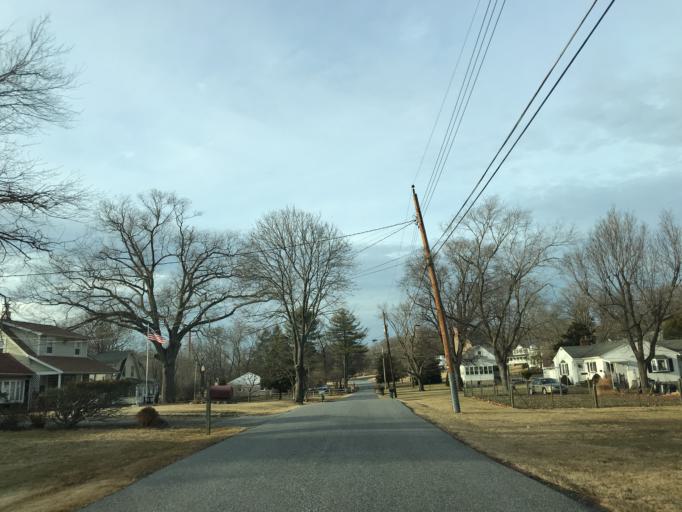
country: US
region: Maryland
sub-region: Baltimore County
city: Kingsville
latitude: 39.4295
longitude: -76.3955
